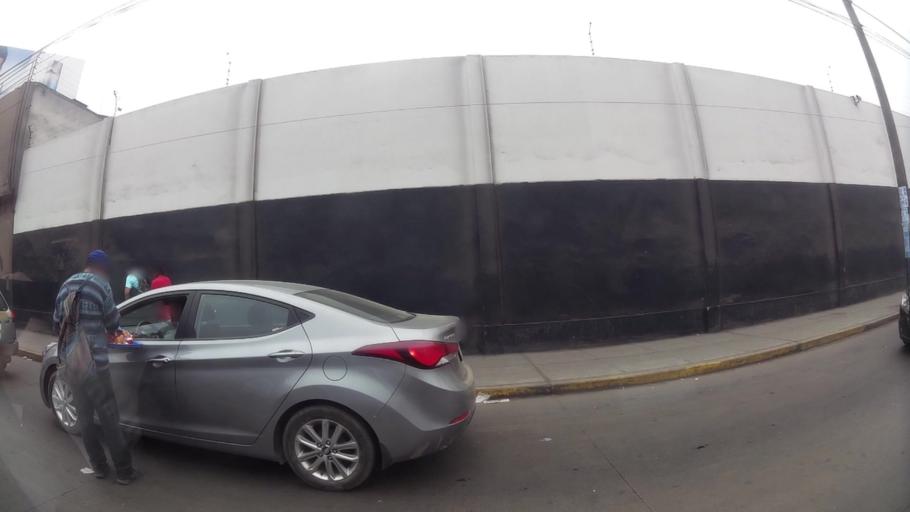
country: PE
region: Lima
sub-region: Lima
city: San Luis
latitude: -12.0616
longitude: -76.9797
